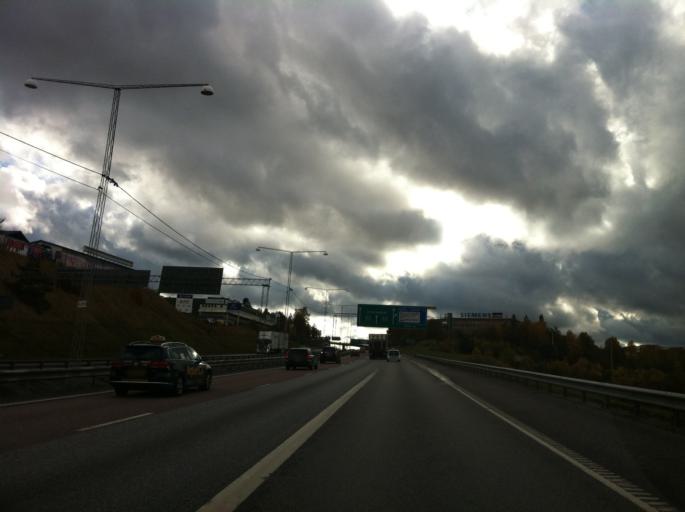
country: SE
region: Stockholm
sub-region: Upplands Vasby Kommun
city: Upplands Vaesby
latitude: 59.5106
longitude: 17.9237
